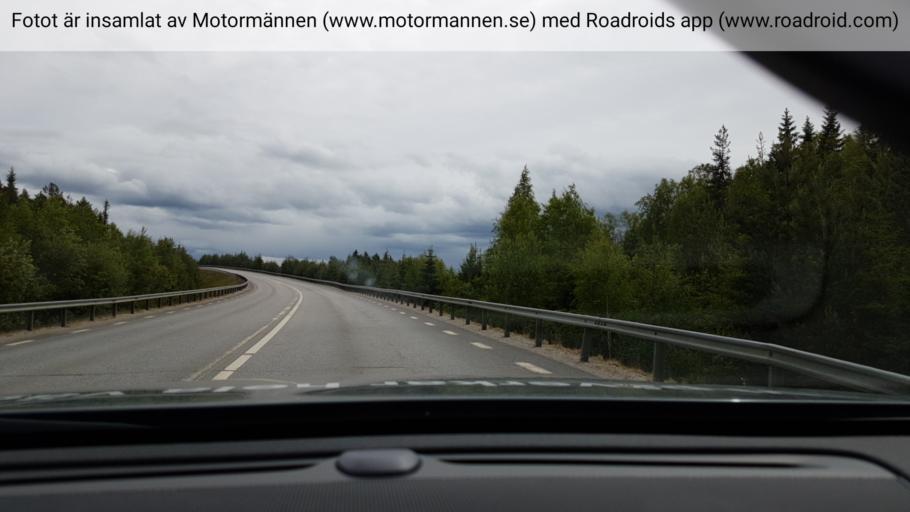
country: SE
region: Vaesterbotten
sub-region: Vannas Kommun
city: Vaennaes
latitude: 64.0101
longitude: 19.6973
